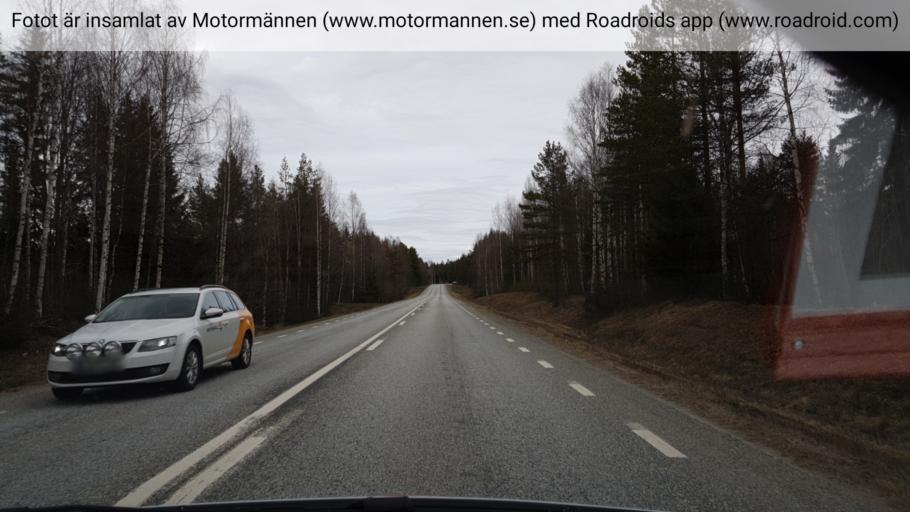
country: SE
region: Vaesternorrland
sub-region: Solleftea Kommun
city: As
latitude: 63.6748
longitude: 16.7987
